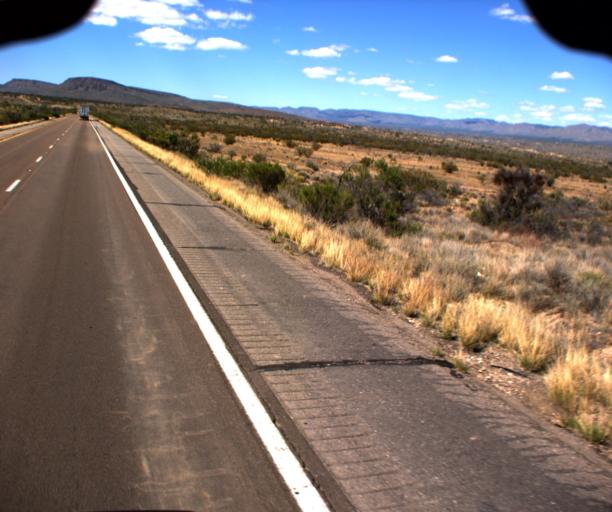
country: US
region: Arizona
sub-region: Mohave County
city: Kingman
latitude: 35.1155
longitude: -113.6661
